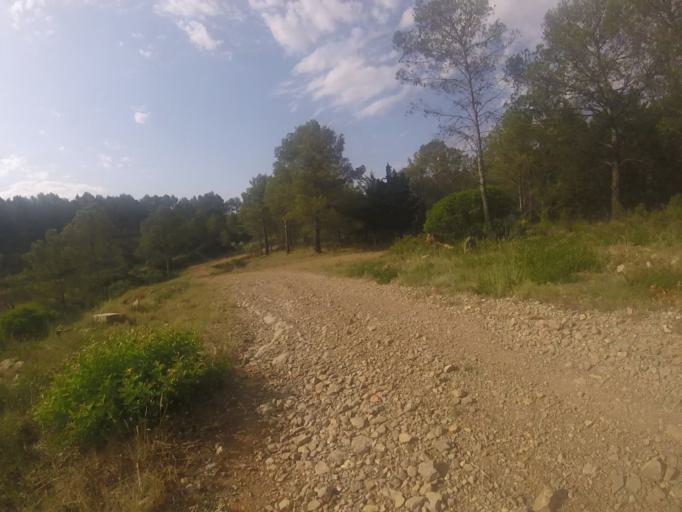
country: ES
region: Valencia
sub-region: Provincia de Castello
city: Cervera del Maestre
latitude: 40.3988
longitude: 0.2056
